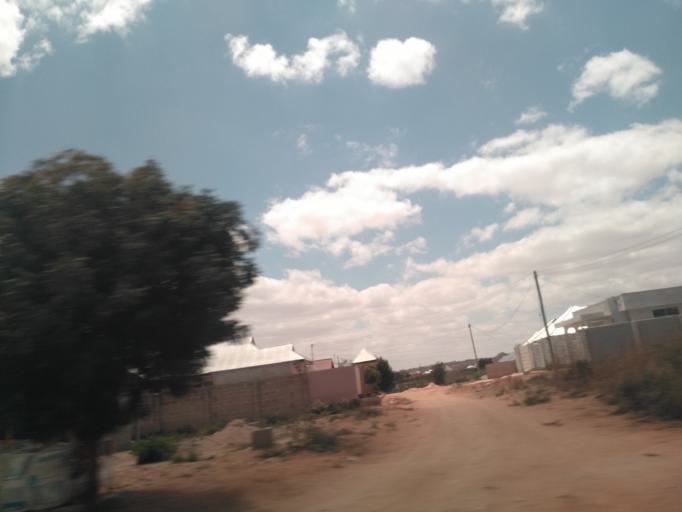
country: TZ
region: Dodoma
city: Kisasa
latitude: -6.1701
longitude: 35.8004
